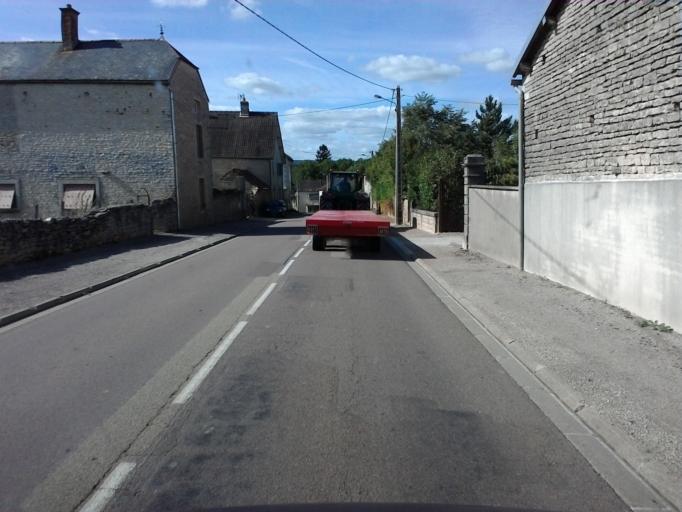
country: FR
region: Bourgogne
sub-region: Departement de la Cote-d'Or
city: Chatillon-sur-Seine
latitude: 47.9149
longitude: 4.6685
